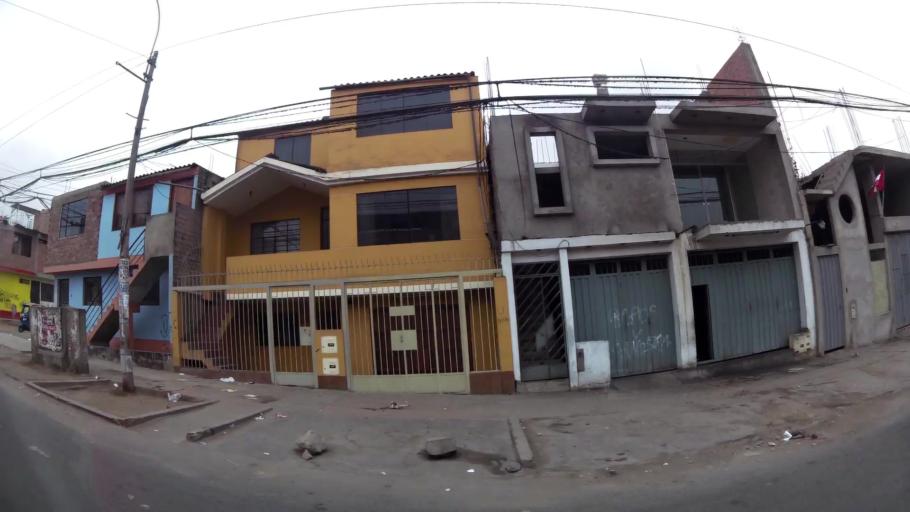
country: PE
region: Lima
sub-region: Lima
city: Surco
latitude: -12.1398
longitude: -76.9623
